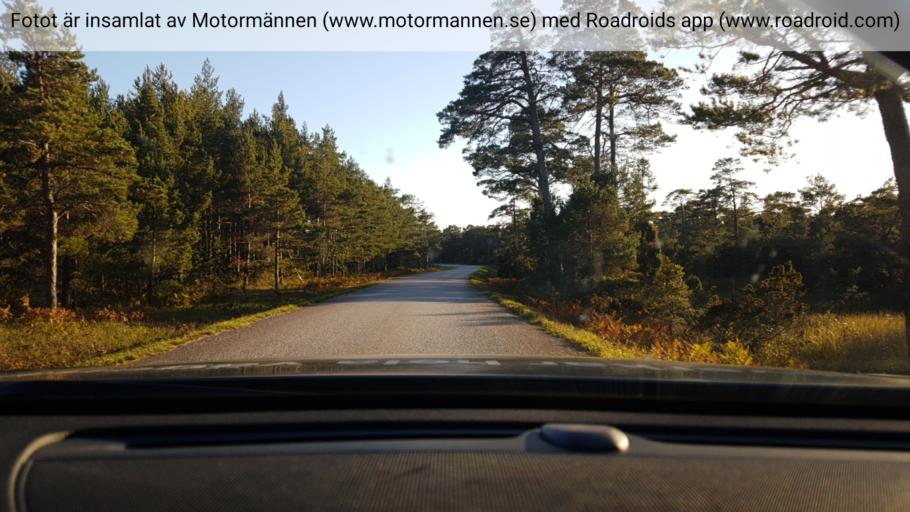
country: SE
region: Gotland
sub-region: Gotland
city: Slite
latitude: 57.8749
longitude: 18.7003
